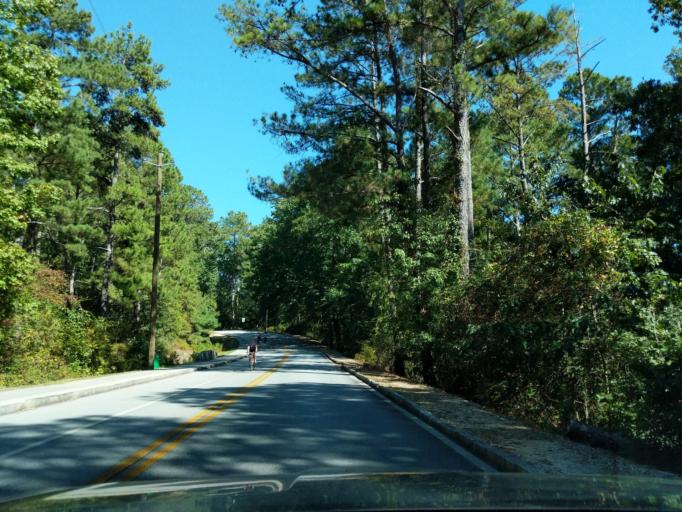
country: US
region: Georgia
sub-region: DeKalb County
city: Stone Mountain
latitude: 33.7987
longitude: -84.1458
